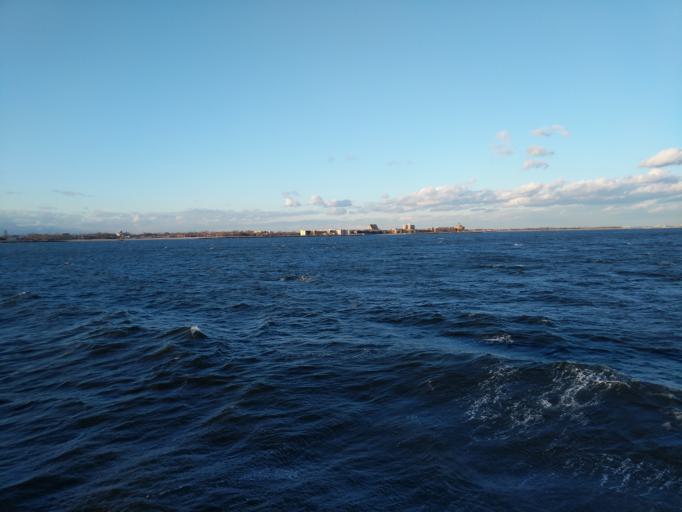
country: US
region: New York
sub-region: Kings County
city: Coney Island
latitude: 40.5633
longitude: -73.9448
